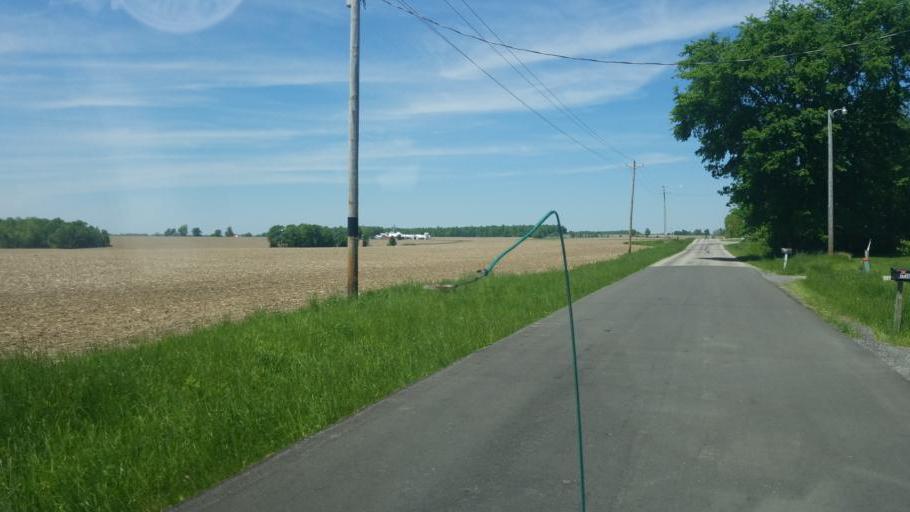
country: US
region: Ohio
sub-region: Huron County
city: Greenwich
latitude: 41.0928
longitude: -82.5372
